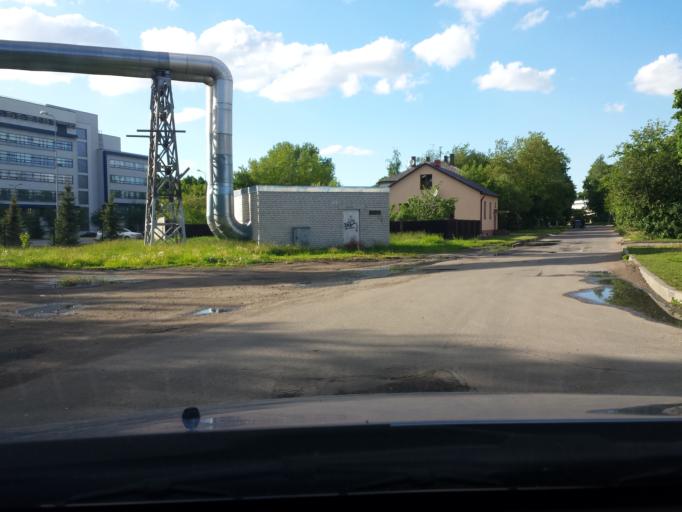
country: LV
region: Riga
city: Jaunciems
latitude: 56.9819
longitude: 24.1600
